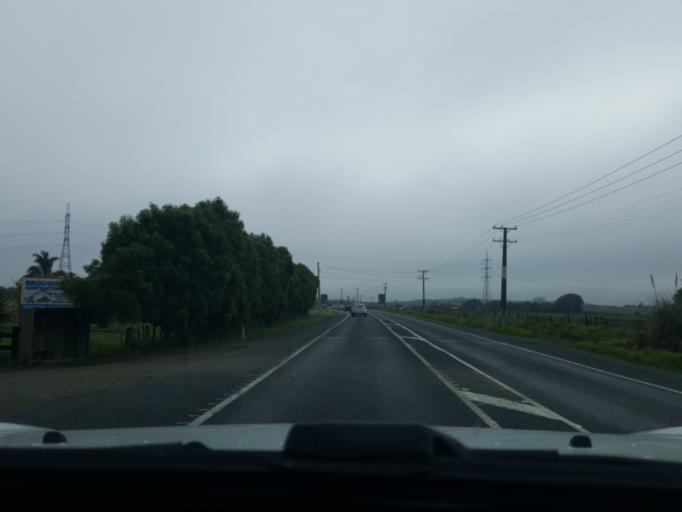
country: NZ
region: Waikato
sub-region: Waikato District
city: Te Kauwhata
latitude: -37.5220
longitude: 175.1615
